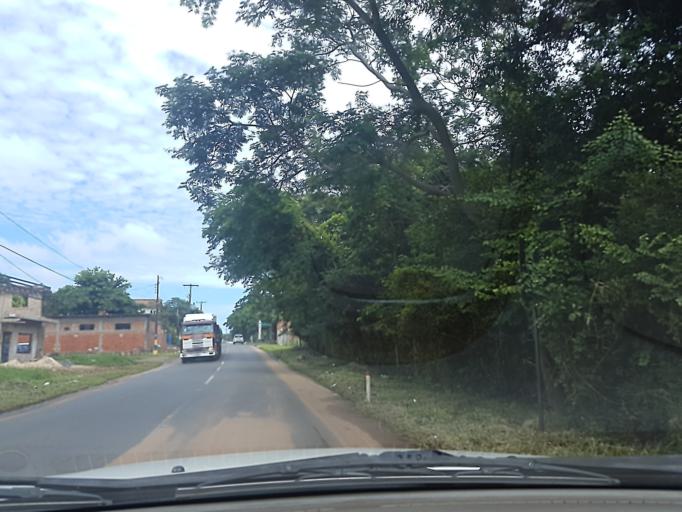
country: PY
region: Central
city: San Lorenzo
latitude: -25.2613
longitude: -57.4830
